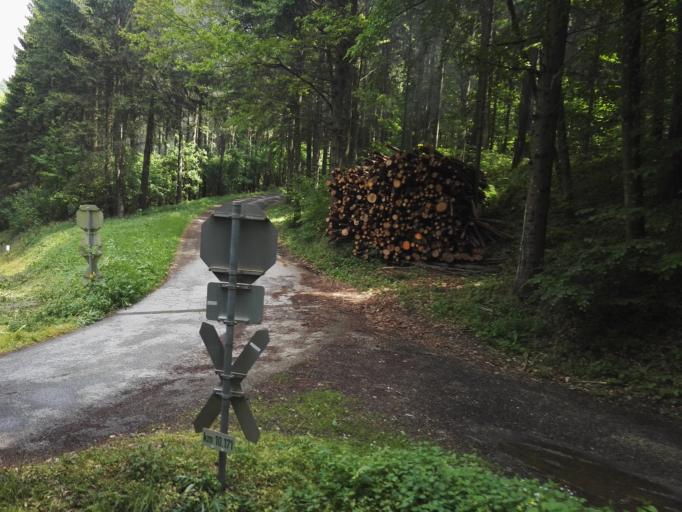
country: AT
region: Styria
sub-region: Politischer Bezirk Weiz
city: Anger
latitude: 47.2511
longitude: 15.7141
